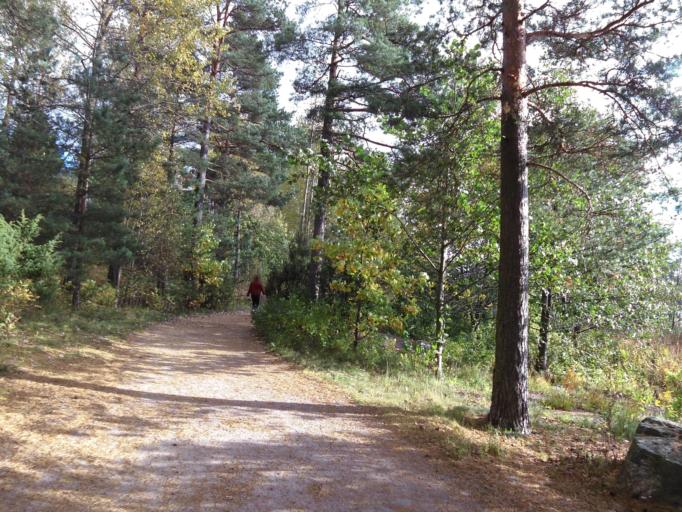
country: FI
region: Uusimaa
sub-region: Helsinki
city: Koukkuniemi
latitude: 60.1541
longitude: 24.7681
